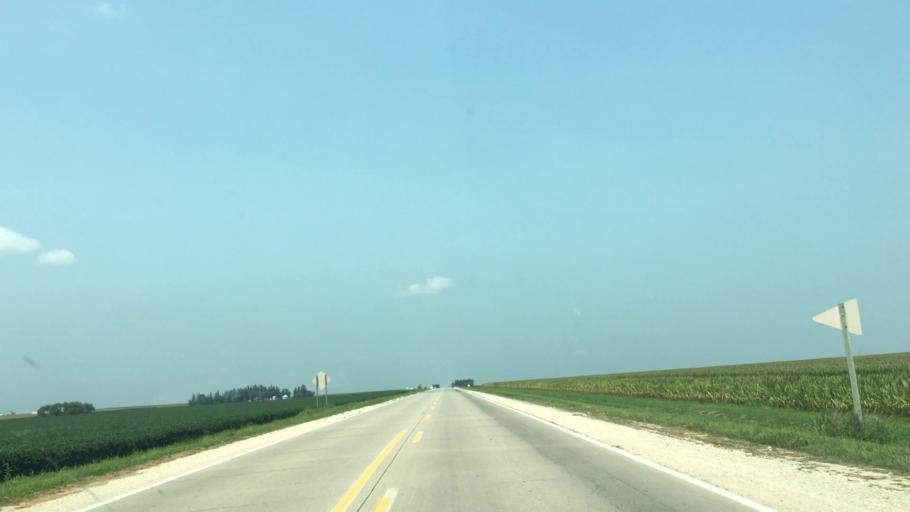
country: US
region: Iowa
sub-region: Fayette County
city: Oelwein
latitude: 42.6889
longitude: -91.8051
